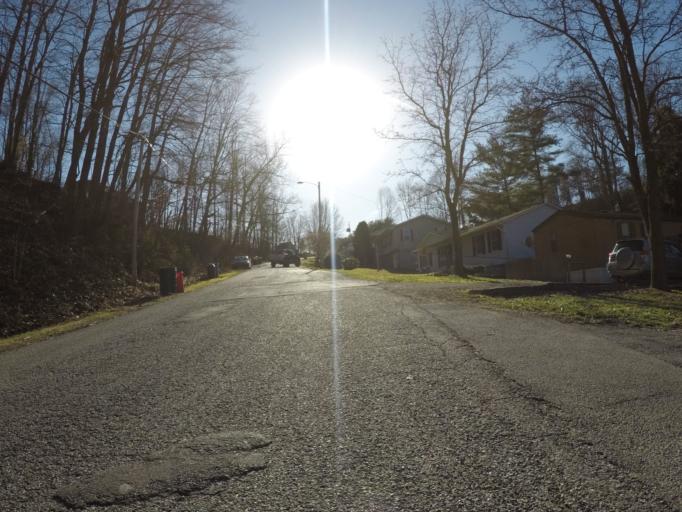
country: US
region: West Virginia
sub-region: Wayne County
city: Ceredo
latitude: 38.3887
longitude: -82.5626
